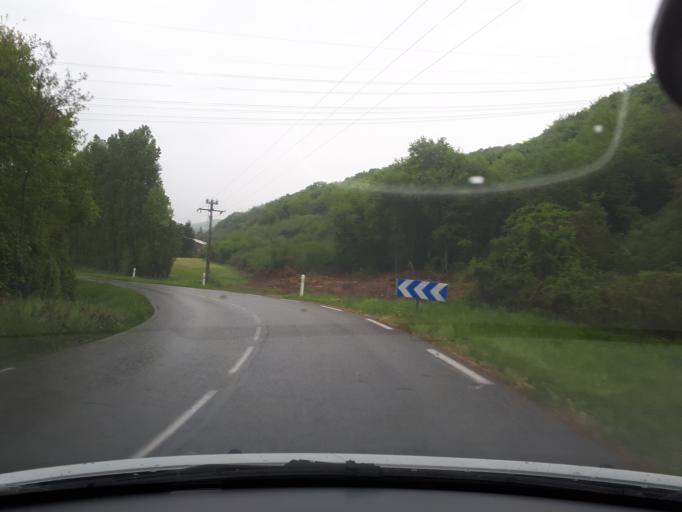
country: FR
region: Rhone-Alpes
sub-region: Departement de l'Isere
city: Frontonas
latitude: 45.6620
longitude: 5.2055
